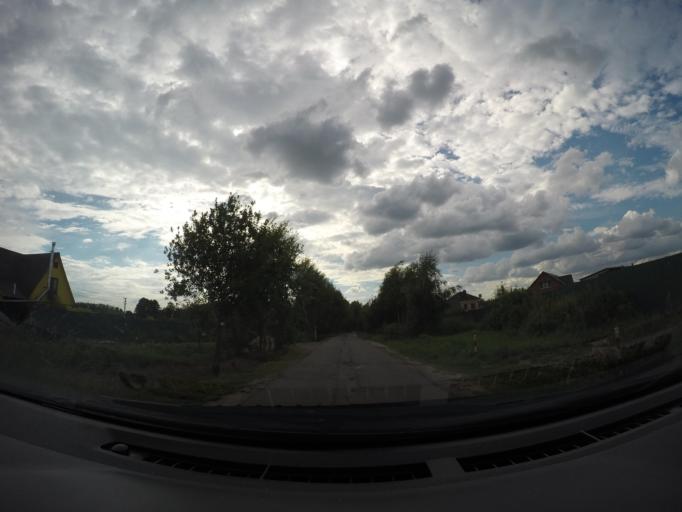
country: RU
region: Moskovskaya
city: Rechitsy
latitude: 55.6067
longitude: 38.5145
